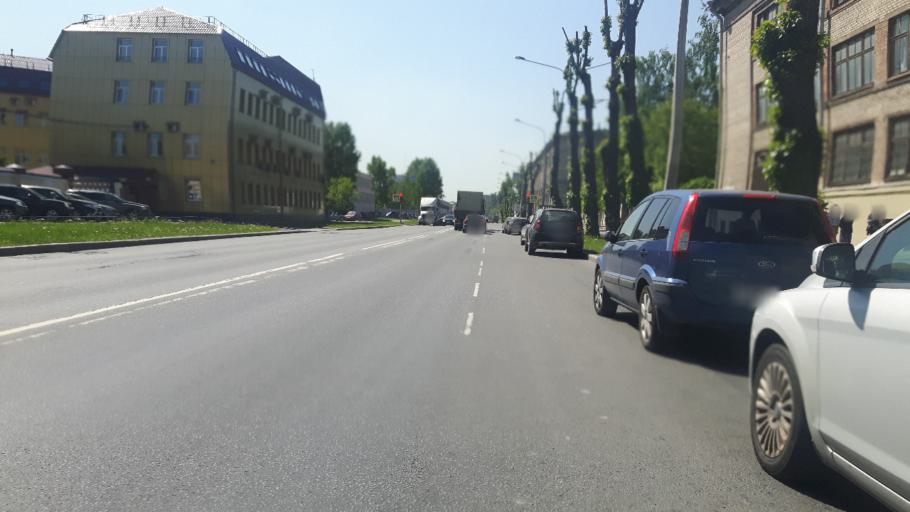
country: RU
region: St.-Petersburg
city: Admiralteisky
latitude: 59.8955
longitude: 30.2859
